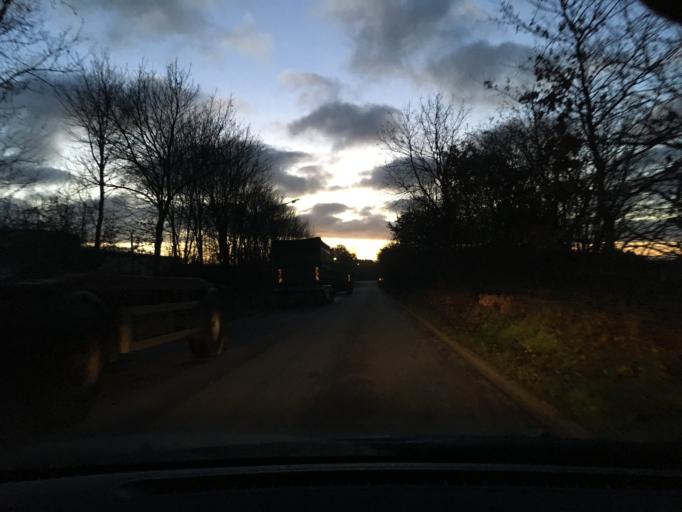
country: DE
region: Schleswig-Holstein
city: Ottenbuttel
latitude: 53.9885
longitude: 9.4990
